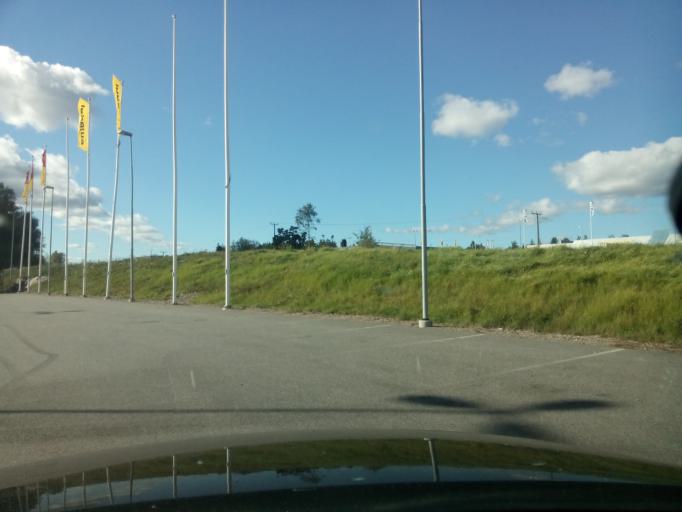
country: SE
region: Soedermanland
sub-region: Nykopings Kommun
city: Nykoping
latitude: 58.7704
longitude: 17.0178
